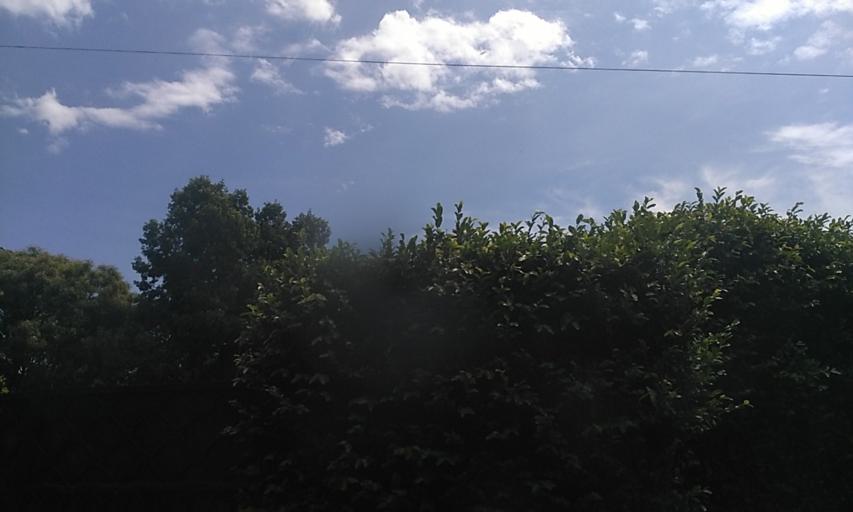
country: UG
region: Central Region
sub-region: Kampala District
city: Kampala
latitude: 0.3332
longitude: 32.5987
